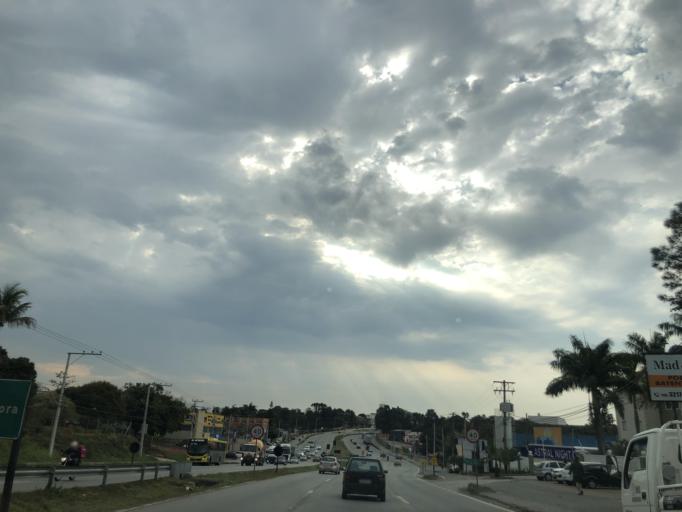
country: BR
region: Sao Paulo
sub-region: Votorantim
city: Votorantim
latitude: -23.5440
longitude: -47.4837
